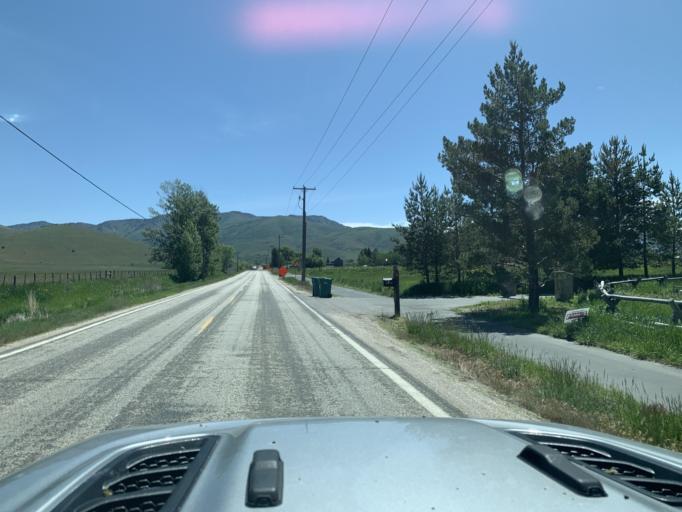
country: US
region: Utah
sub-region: Weber County
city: Wolf Creek
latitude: 41.2932
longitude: -111.7830
